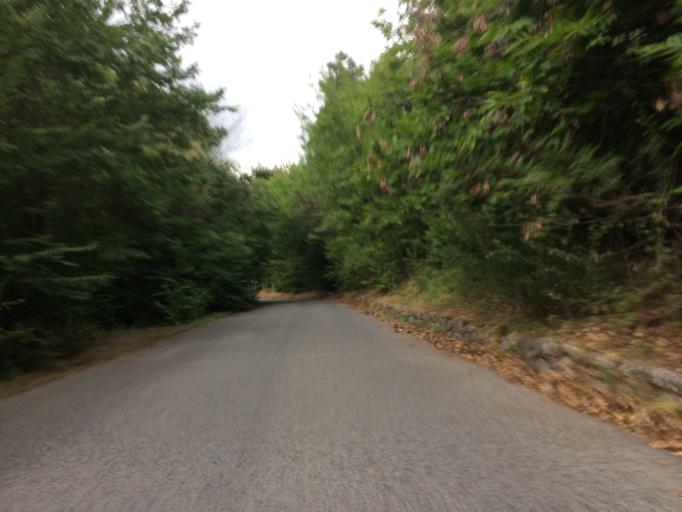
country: IT
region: Liguria
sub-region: Provincia di Imperia
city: Triora
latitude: 43.9831
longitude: 7.7602
